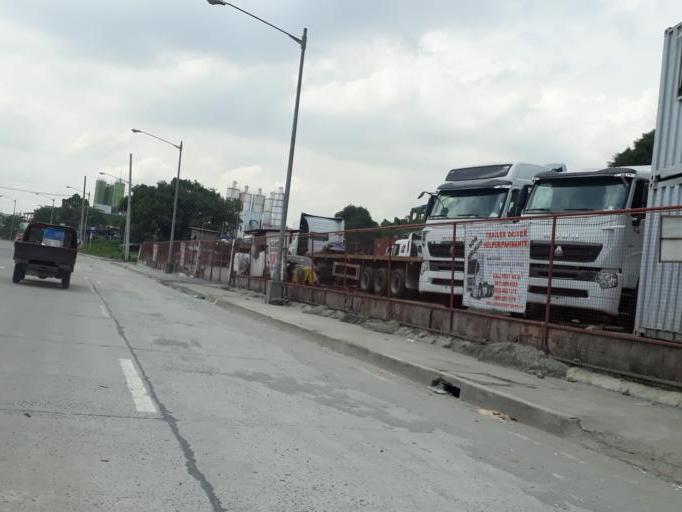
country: PH
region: Calabarzon
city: Bagong Pagasa
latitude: 14.7006
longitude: 121.0158
